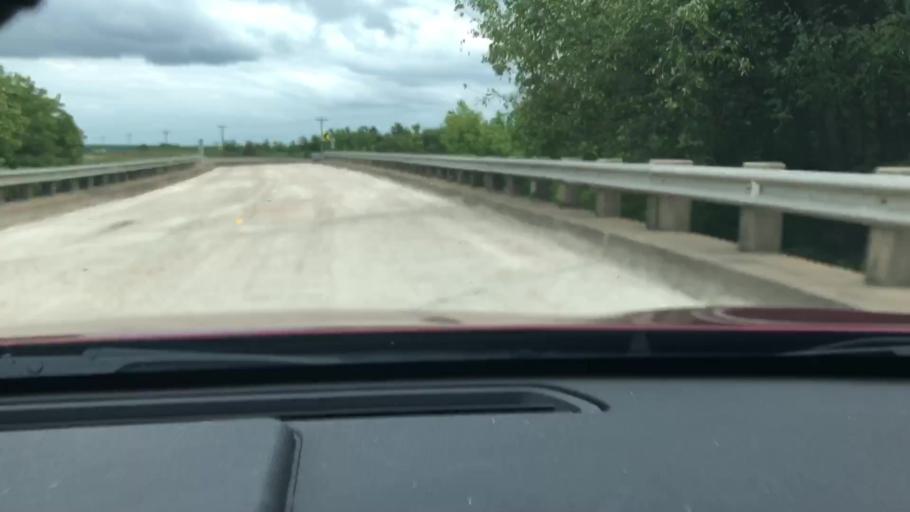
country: US
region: Arkansas
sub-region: Miller County
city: Texarkana
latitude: 33.4132
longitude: -93.8078
